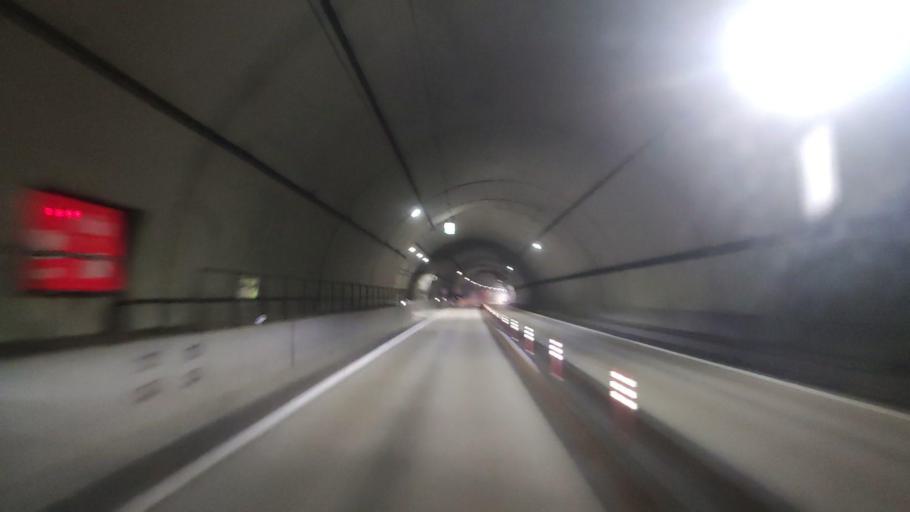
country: JP
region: Wakayama
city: Tanabe
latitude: 33.5930
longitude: 135.4375
